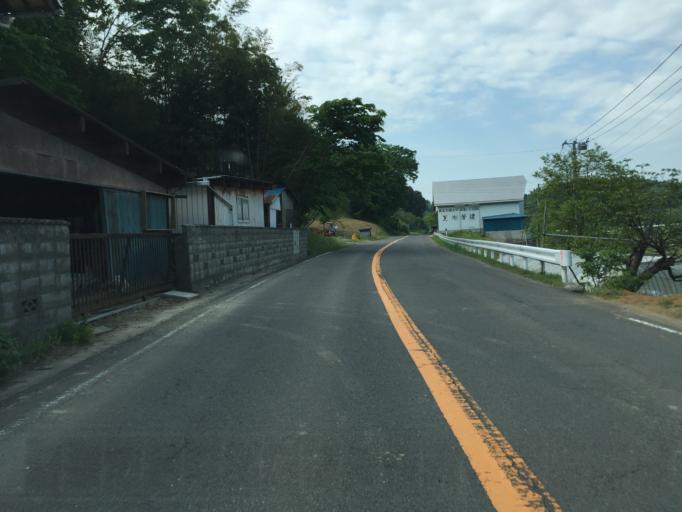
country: JP
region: Fukushima
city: Fukushima-shi
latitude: 37.6745
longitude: 140.5268
